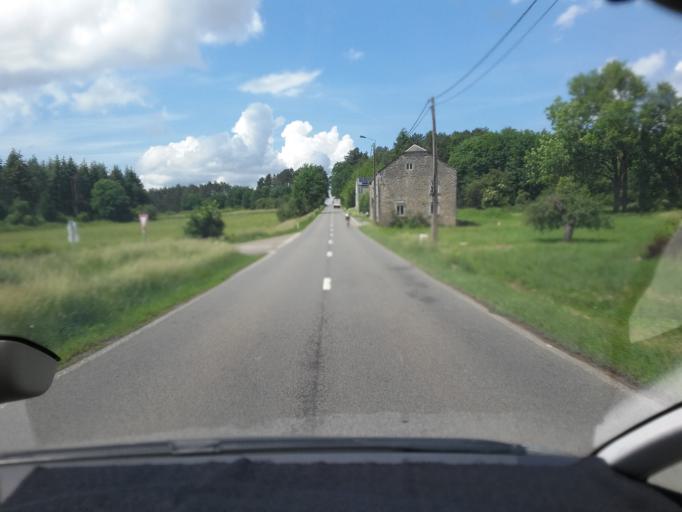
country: BE
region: Wallonia
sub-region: Province de Namur
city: Rochefort
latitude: 50.1303
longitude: 5.2364
